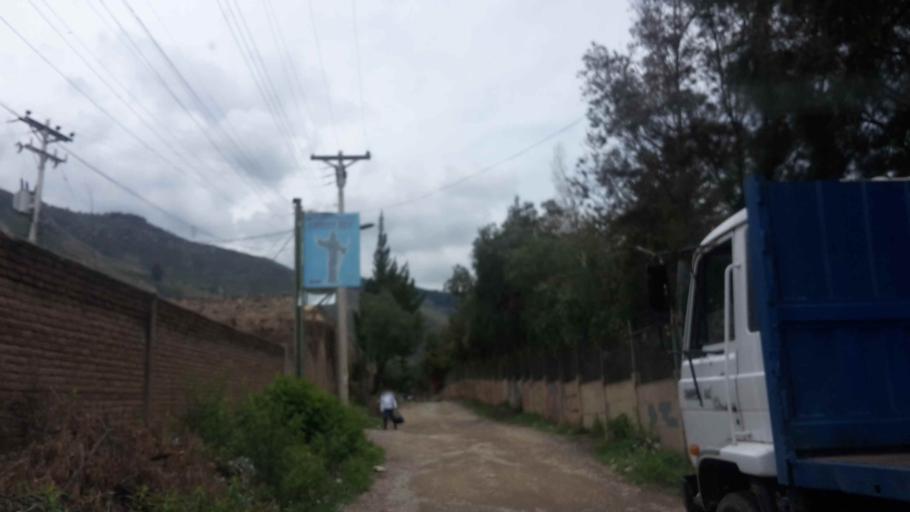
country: BO
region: Cochabamba
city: Cochabamba
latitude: -17.3373
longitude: -66.1859
